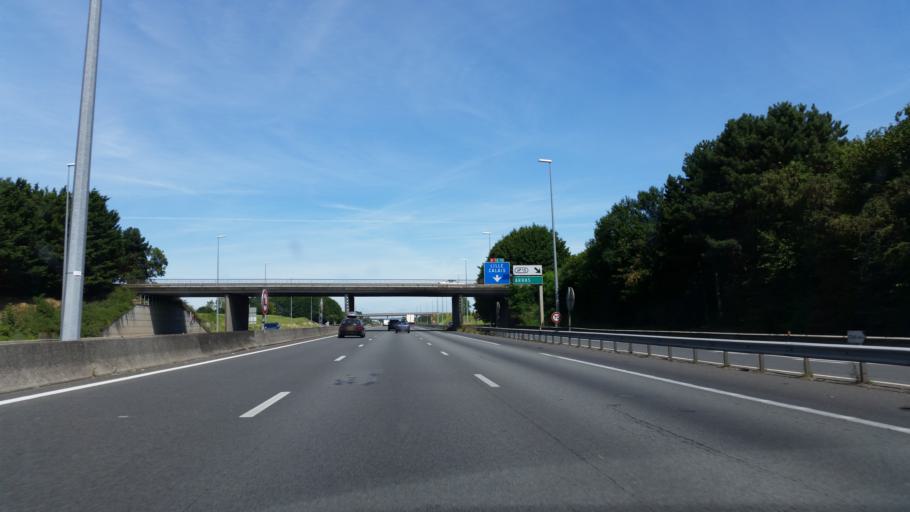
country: FR
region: Nord-Pas-de-Calais
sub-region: Departement du Pas-de-Calais
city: Fampoux
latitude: 50.2658
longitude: 2.8663
